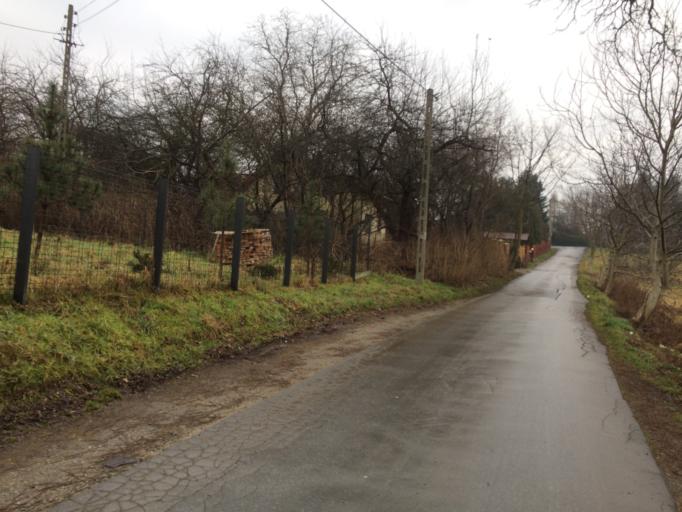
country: PL
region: Lesser Poland Voivodeship
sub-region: Powiat wielicki
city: Czarnochowice
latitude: 50.0043
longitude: 20.0386
